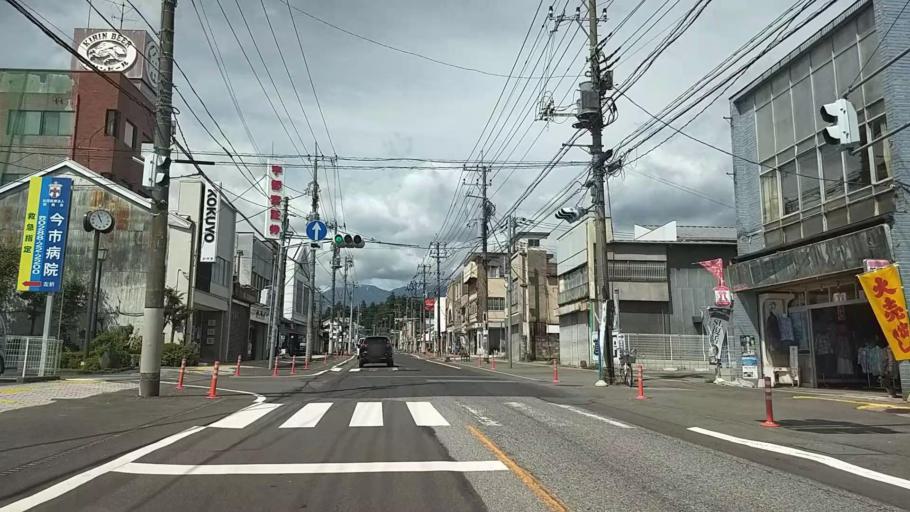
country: JP
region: Tochigi
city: Imaichi
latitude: 36.7249
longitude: 139.6862
